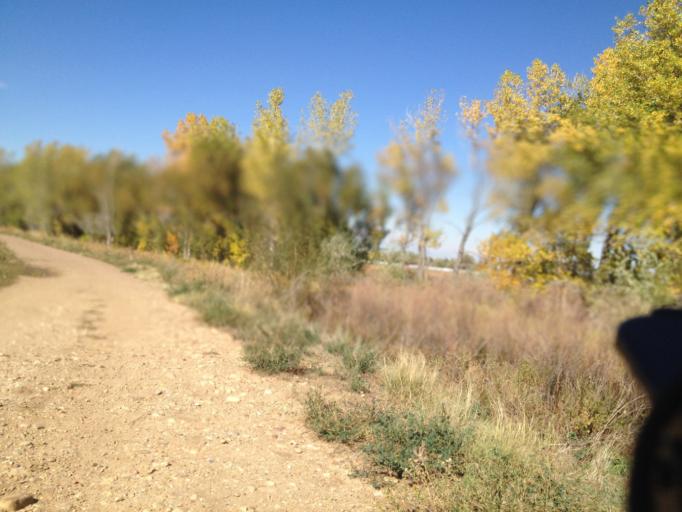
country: US
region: Colorado
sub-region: Boulder County
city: Boulder
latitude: 39.9770
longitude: -105.2250
